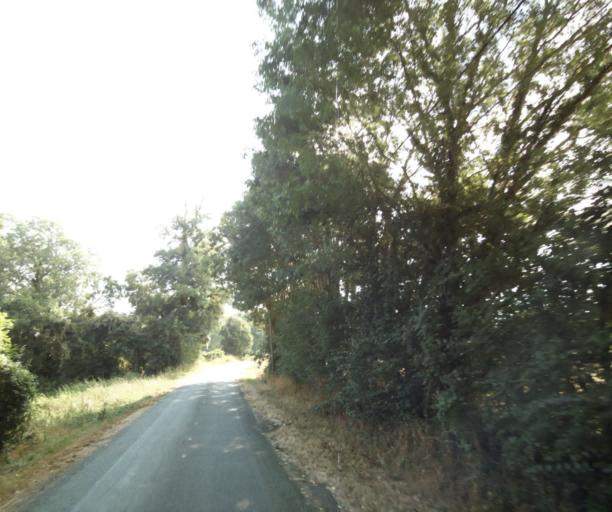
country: FR
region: Poitou-Charentes
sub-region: Departement de la Charente-Maritime
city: Tonnay-Charente
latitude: 45.9648
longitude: -0.8617
